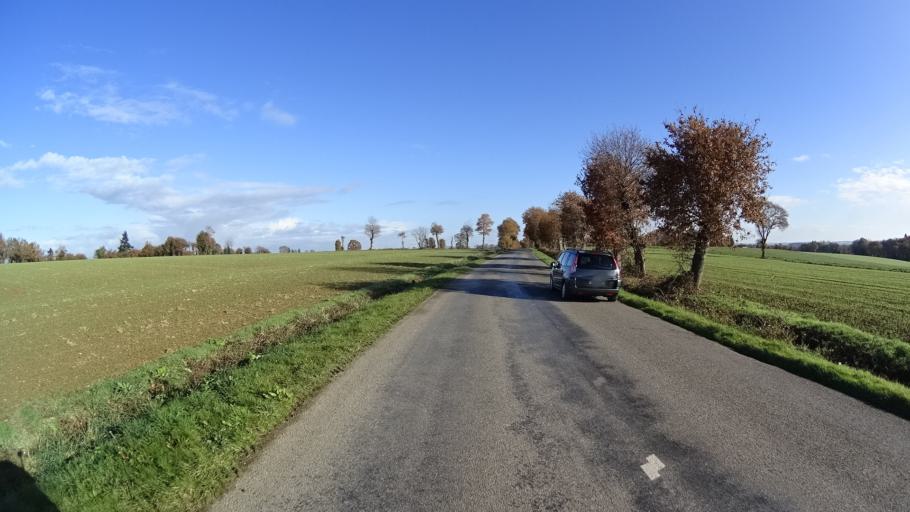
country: FR
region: Brittany
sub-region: Departement du Morbihan
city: Saint-Martin-sur-Oust
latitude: 47.7931
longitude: -2.2060
